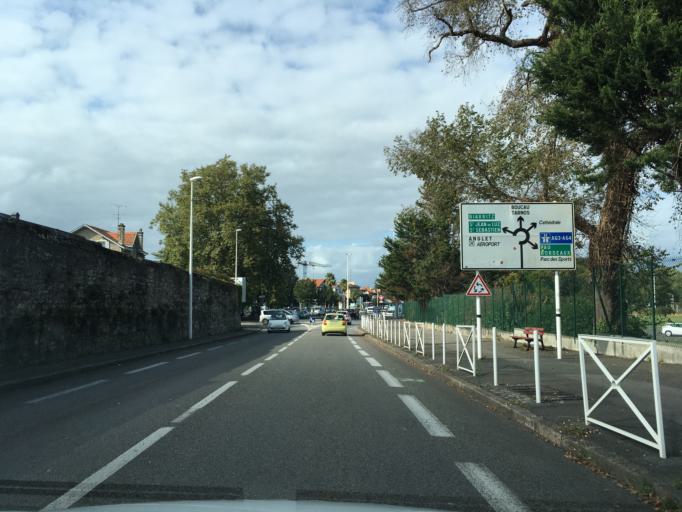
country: FR
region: Aquitaine
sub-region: Departement des Pyrenees-Atlantiques
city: Bayonne
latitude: 43.4862
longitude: -1.4828
